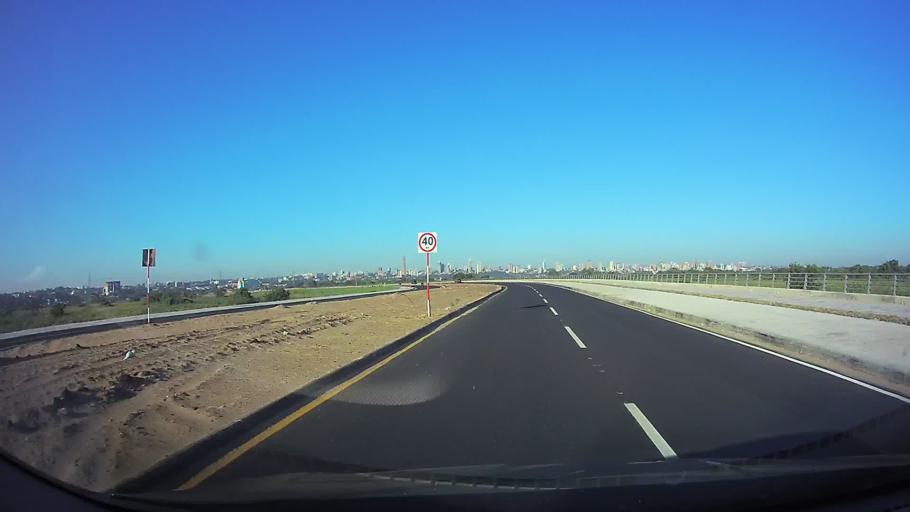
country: PY
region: Asuncion
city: Asuncion
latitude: -25.2548
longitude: -57.6072
